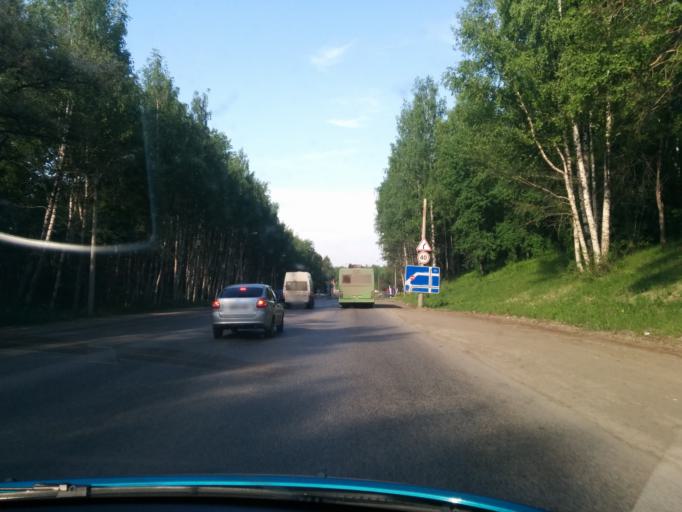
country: RU
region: Perm
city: Kondratovo
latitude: 58.0437
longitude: 56.0564
